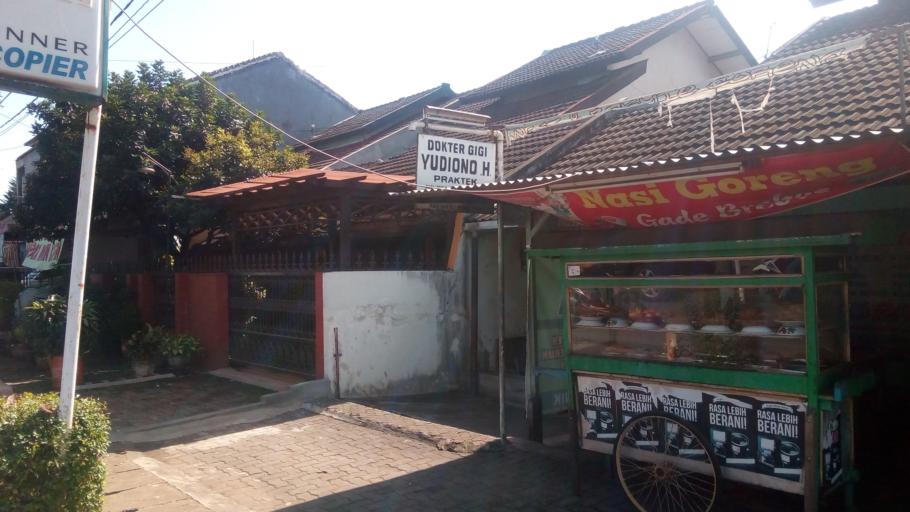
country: ID
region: Central Java
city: Ungaran
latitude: -7.0677
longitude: 110.4183
